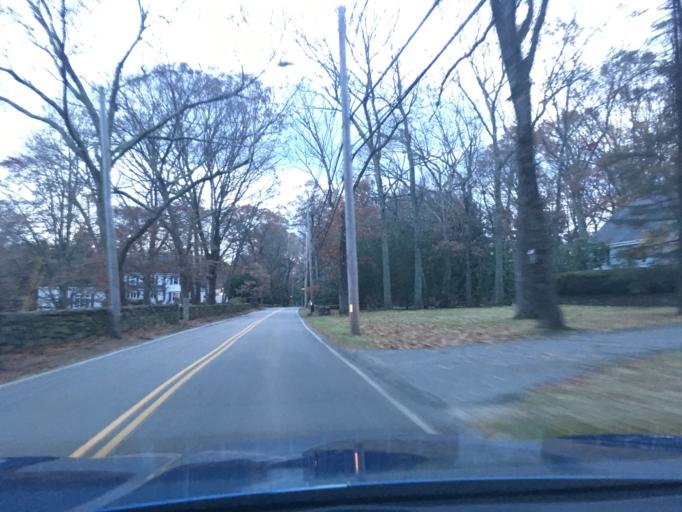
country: US
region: Rhode Island
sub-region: Kent County
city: East Greenwich
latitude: 41.6716
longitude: -71.4578
